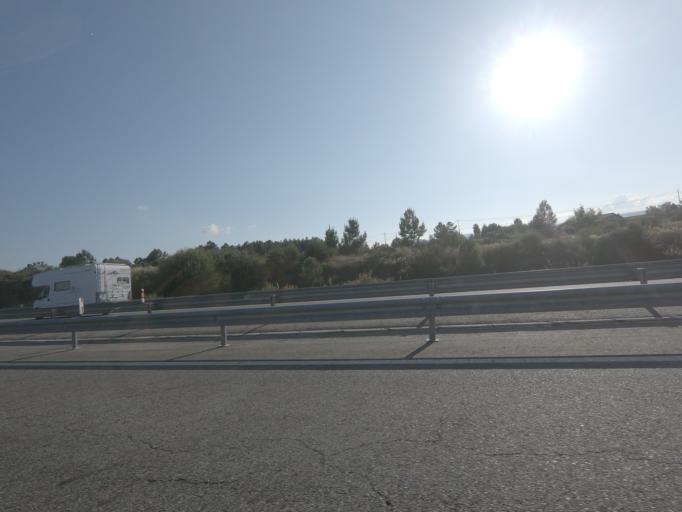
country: PT
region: Vila Real
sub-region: Chaves
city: Chaves
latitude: 41.8107
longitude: -7.4126
